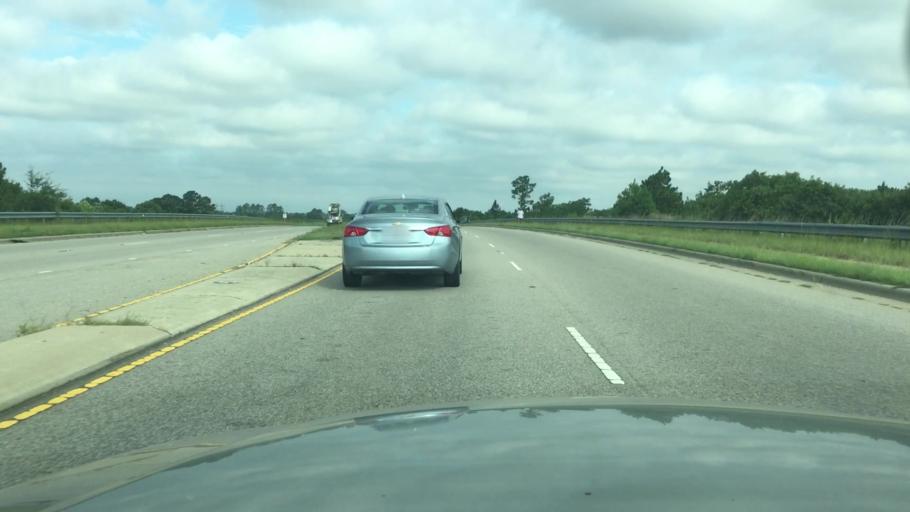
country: US
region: North Carolina
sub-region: Cumberland County
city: Hope Mills
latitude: 34.9894
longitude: -78.9378
